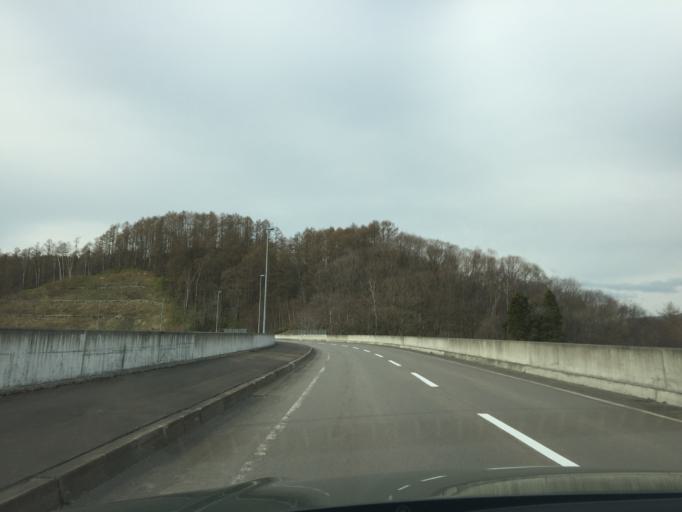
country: JP
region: Hokkaido
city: Utashinai
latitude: 43.5192
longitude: 142.0242
